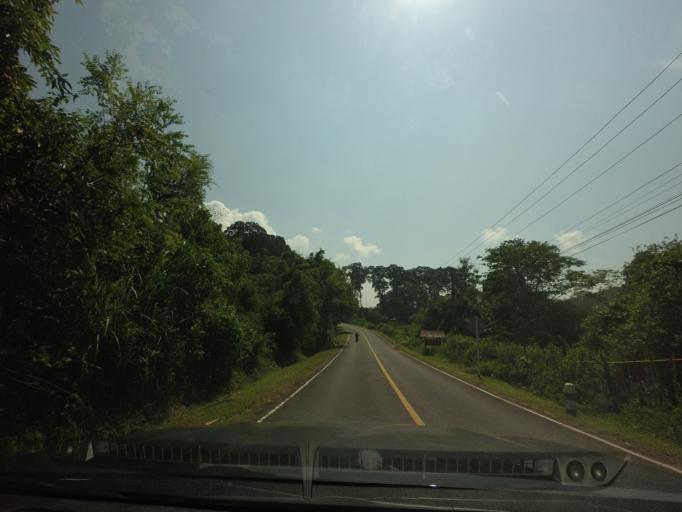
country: TH
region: Nan
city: Bo Kluea
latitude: 19.0661
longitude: 101.1614
